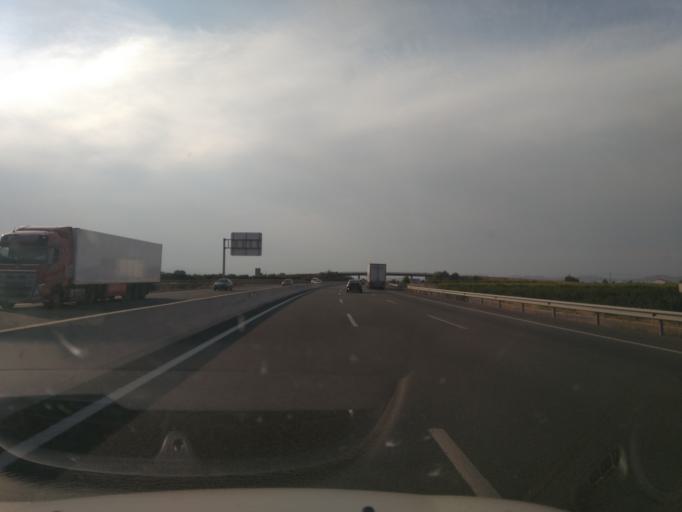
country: ES
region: Valencia
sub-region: Provincia de Valencia
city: Torrent
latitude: 39.4250
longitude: -0.5227
